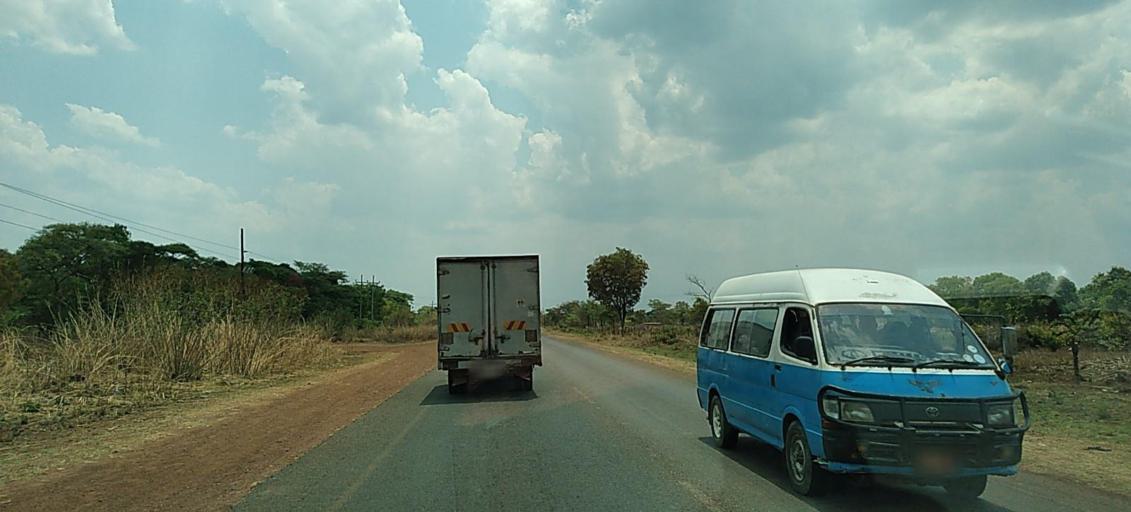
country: ZM
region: Copperbelt
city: Kalulushi
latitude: -12.8357
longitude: 27.9527
